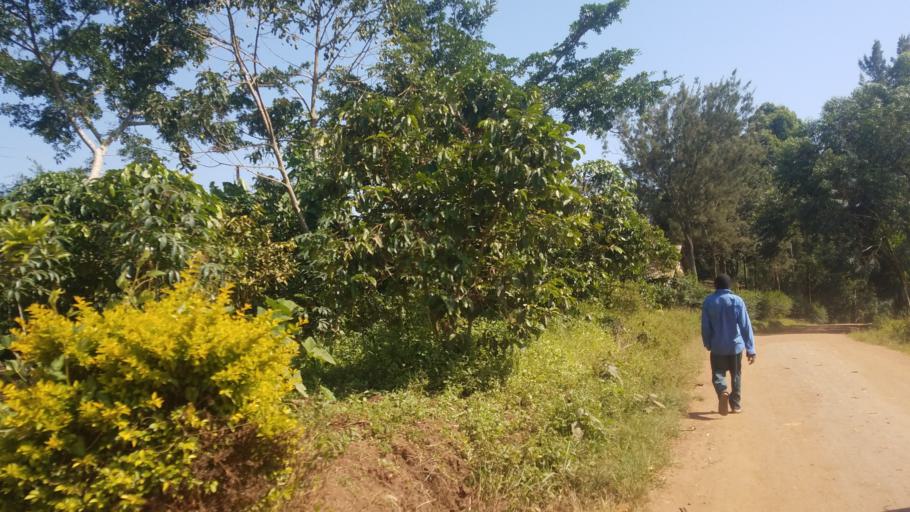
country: UG
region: Central Region
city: Masaka
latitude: -0.3275
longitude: 31.7090
